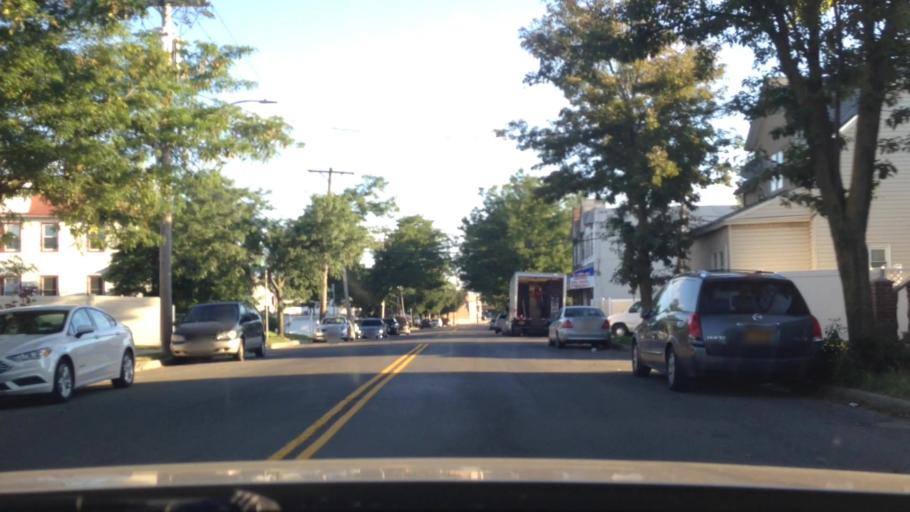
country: US
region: New York
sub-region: Nassau County
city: South Valley Stream
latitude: 40.6630
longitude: -73.7292
